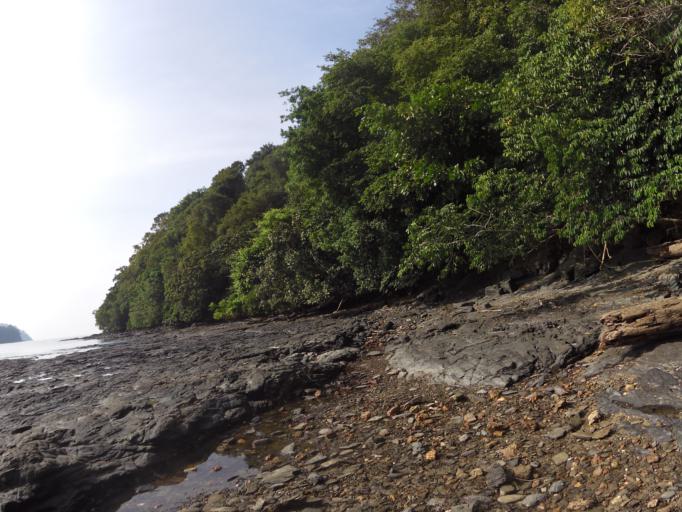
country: MY
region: Kedah
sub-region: Langkawi
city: Kuah
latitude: 6.2193
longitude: 99.7194
